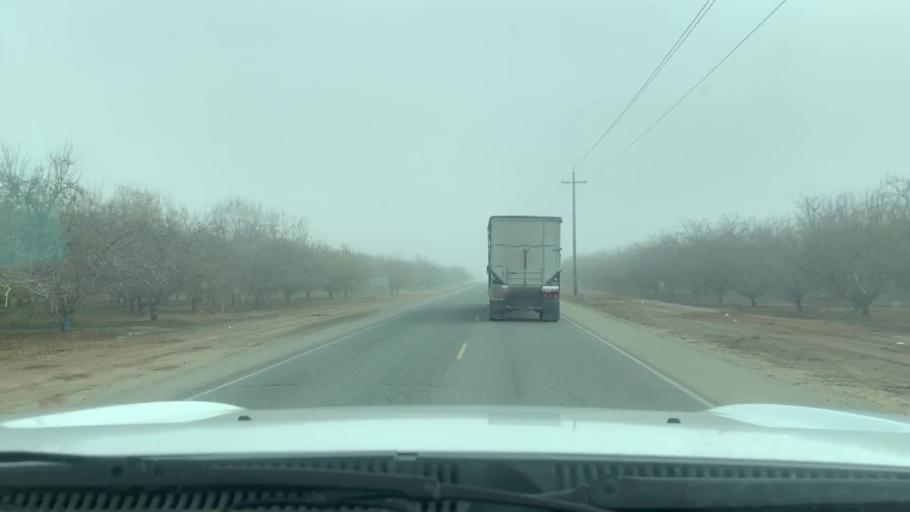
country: US
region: California
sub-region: Kern County
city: Buttonwillow
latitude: 35.5007
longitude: -119.5147
